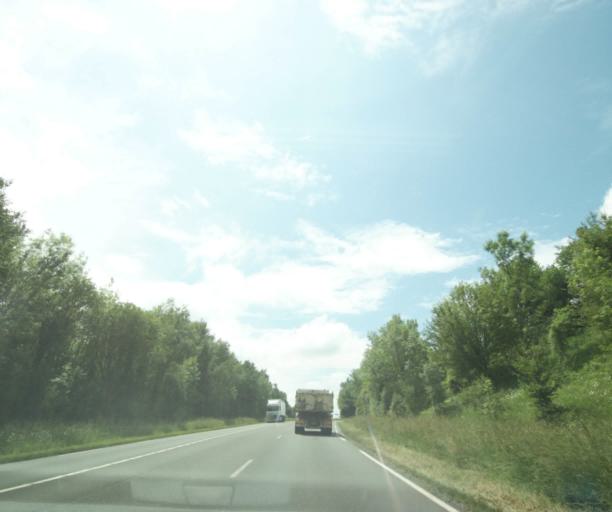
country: FR
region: Poitou-Charentes
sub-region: Departement des Deux-Sevres
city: Champdeniers-Saint-Denis
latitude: 46.4769
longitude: -0.3612
